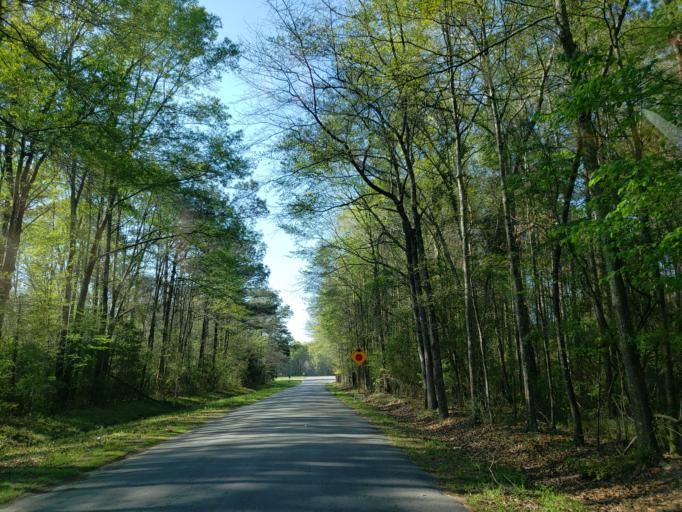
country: US
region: Mississippi
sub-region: Smith County
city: Taylorsville
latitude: 31.7026
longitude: -89.4149
